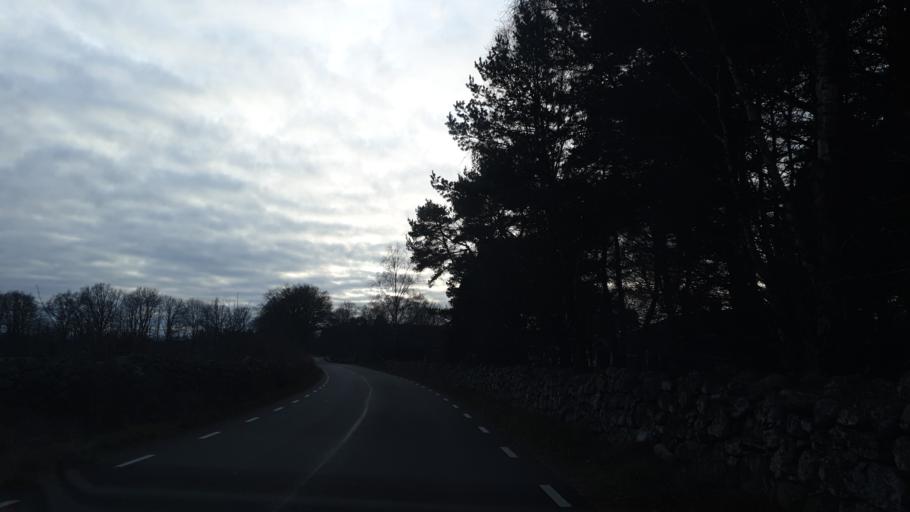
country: SE
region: Kalmar
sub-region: Torsas Kommun
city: Torsas
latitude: 56.2299
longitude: 15.9945
